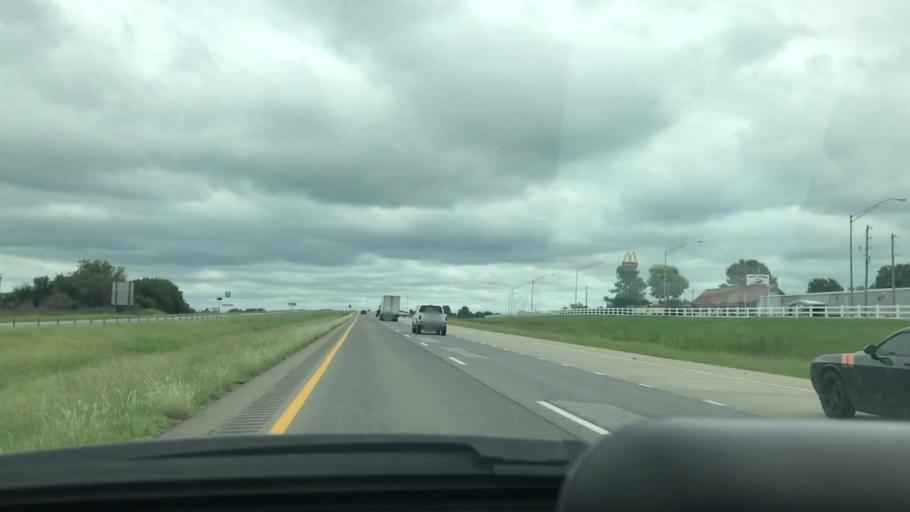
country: US
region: Oklahoma
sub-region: McIntosh County
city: Checotah
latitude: 35.4699
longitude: -95.5385
